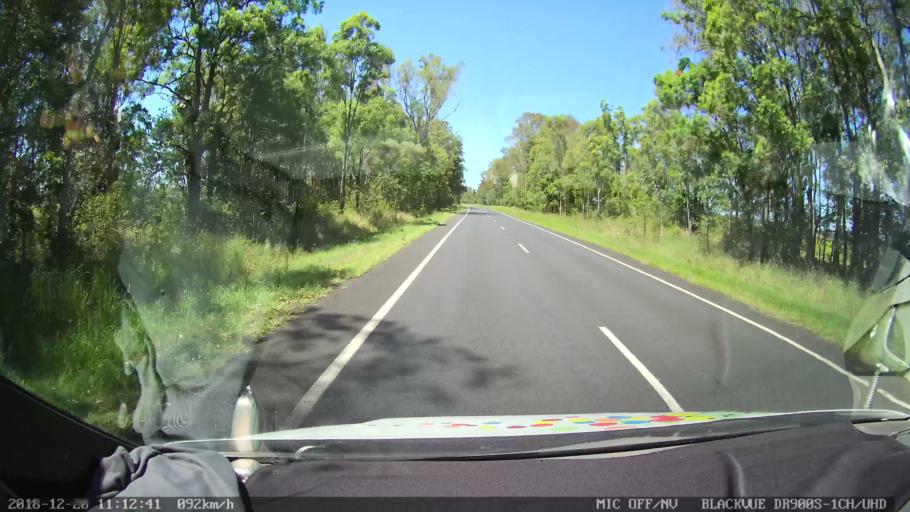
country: AU
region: New South Wales
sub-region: Richmond Valley
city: Casino
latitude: -28.9775
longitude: 153.0102
